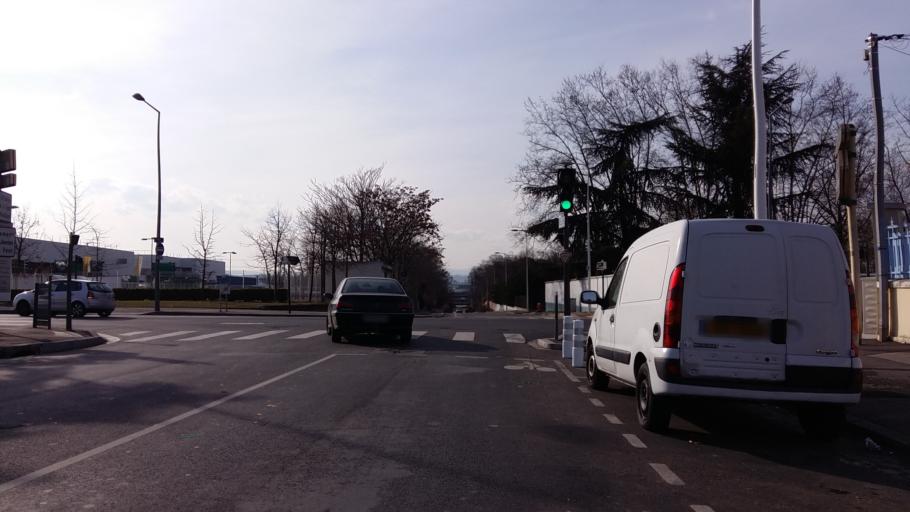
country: FR
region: Rhone-Alpes
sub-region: Departement du Rhone
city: Saint-Fons
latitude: 45.7194
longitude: 4.8549
